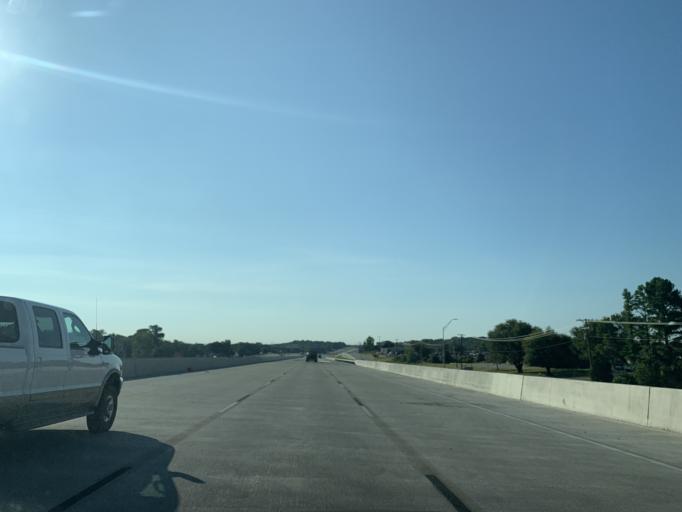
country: US
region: Texas
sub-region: Tarrant County
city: Lakeside
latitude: 32.8551
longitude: -97.5119
